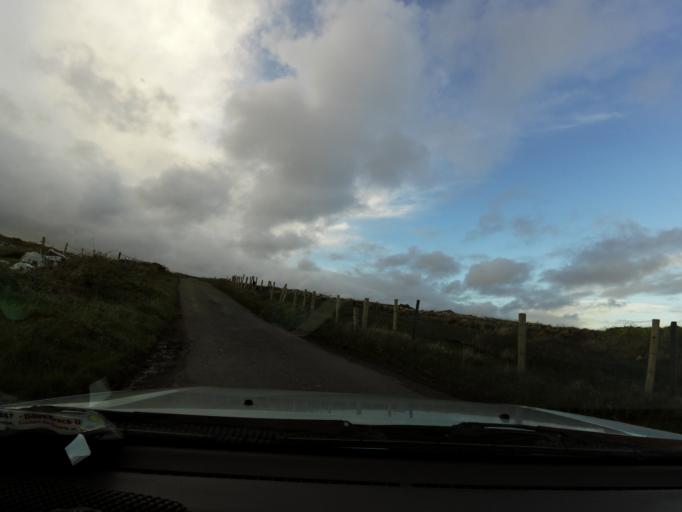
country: IE
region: Munster
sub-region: An Clar
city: Kilrush
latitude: 52.9492
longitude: -9.4437
